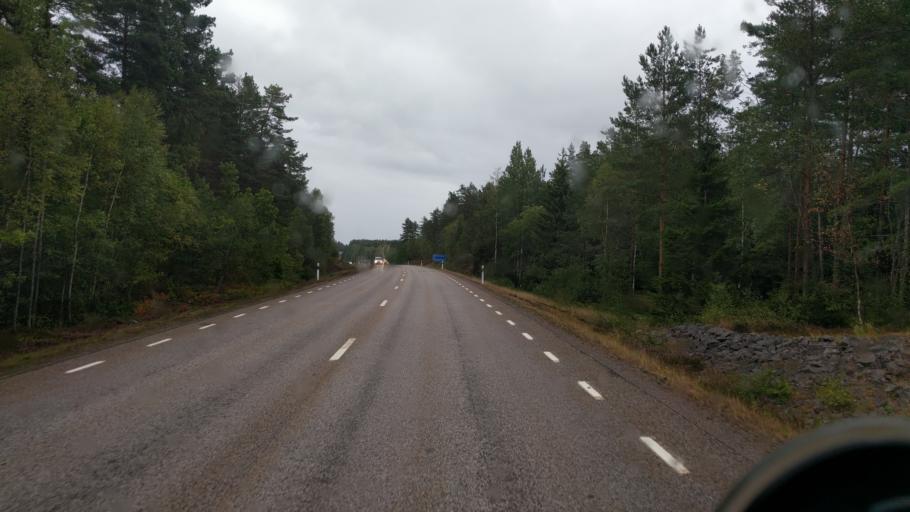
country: SE
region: Kalmar
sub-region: Vasterviks Kommun
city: Ankarsrum
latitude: 57.7050
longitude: 16.3244
